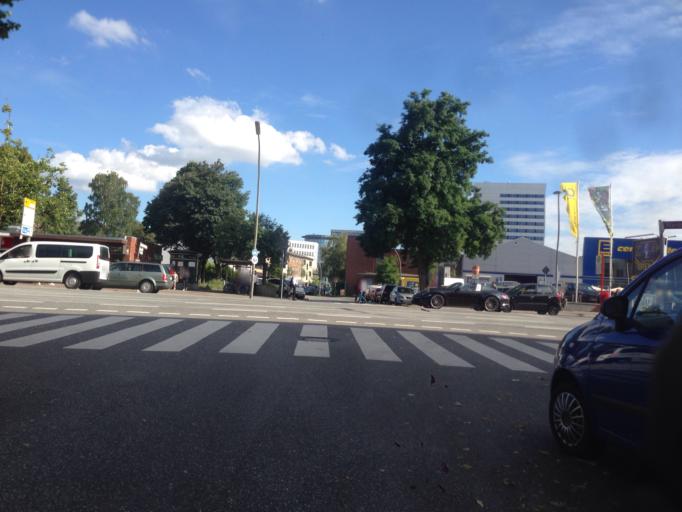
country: DE
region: Hamburg
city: Marienthal
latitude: 53.5704
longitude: 10.0586
